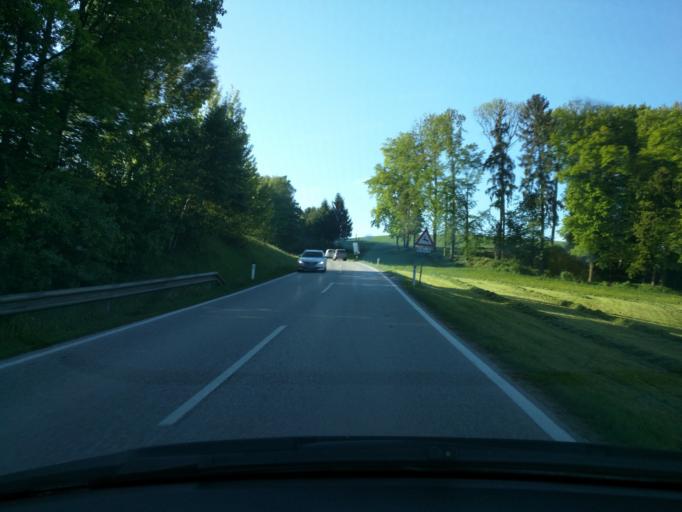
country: AT
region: Lower Austria
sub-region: Politischer Bezirk Amstetten
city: Ferschnitz
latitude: 48.1149
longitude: 15.0130
